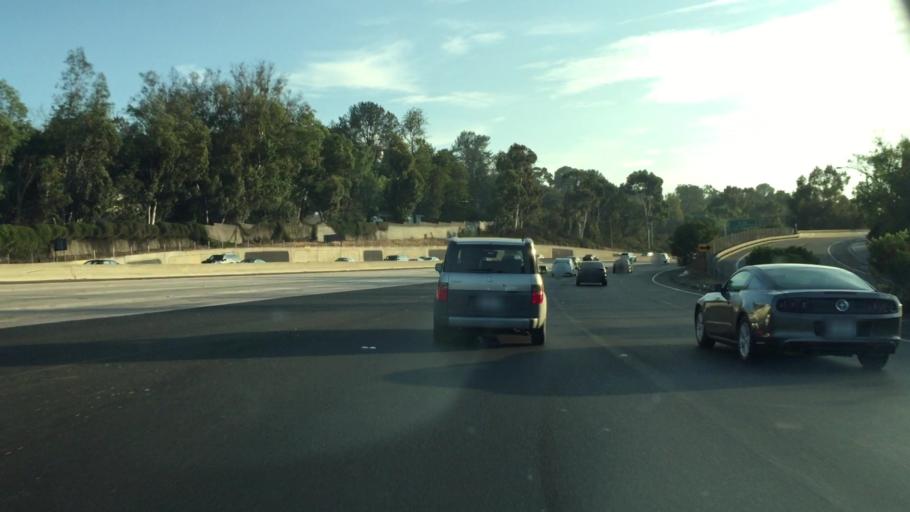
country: US
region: California
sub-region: San Diego County
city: Casa de Oro-Mount Helix
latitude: 32.7798
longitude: -116.9840
